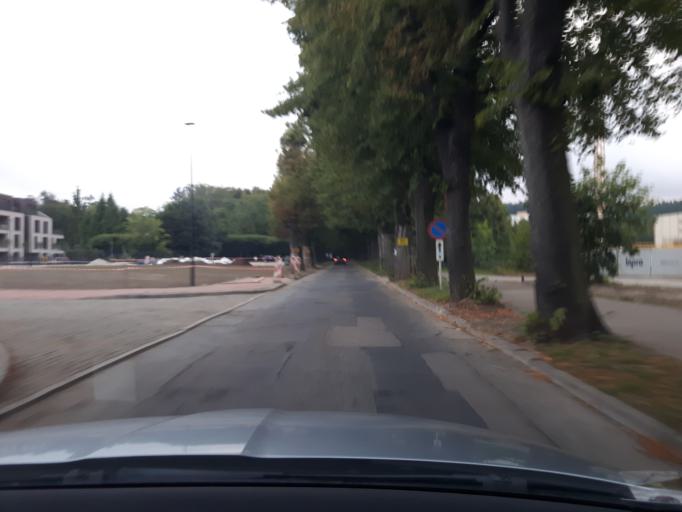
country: PL
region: Pomeranian Voivodeship
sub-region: Sopot
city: Sopot
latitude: 54.4140
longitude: 18.5651
